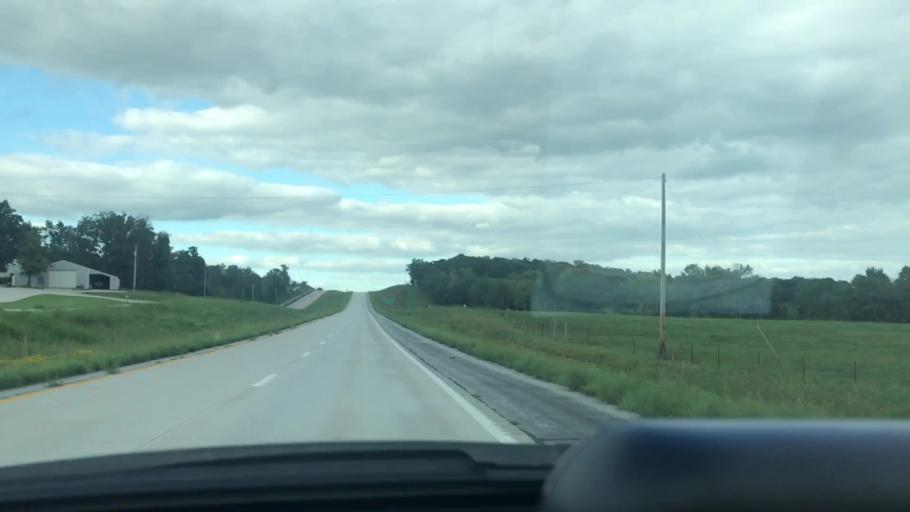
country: US
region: Missouri
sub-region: Benton County
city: Lincoln
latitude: 38.4368
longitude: -93.3013
